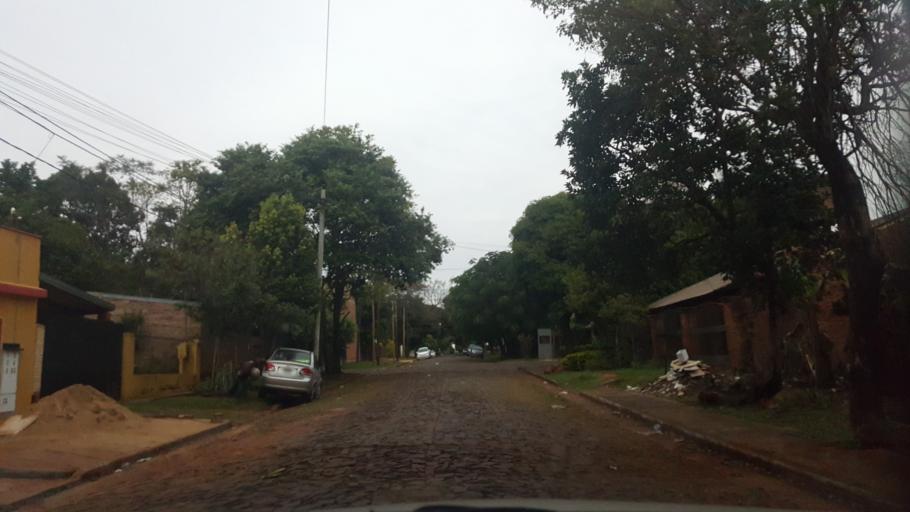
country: AR
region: Misiones
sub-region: Departamento de Capital
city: Posadas
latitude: -27.3841
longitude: -55.9199
